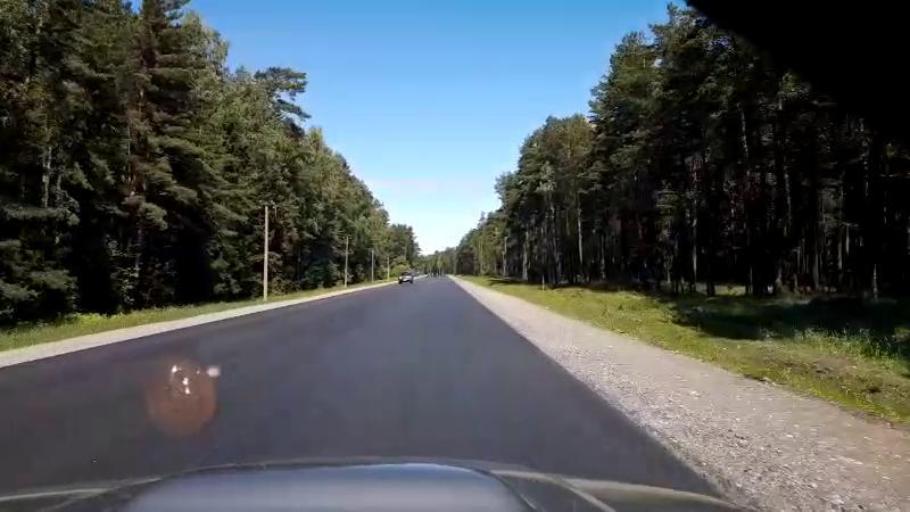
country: LV
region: Salacgrivas
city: Ainazi
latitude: 57.8171
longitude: 24.3472
